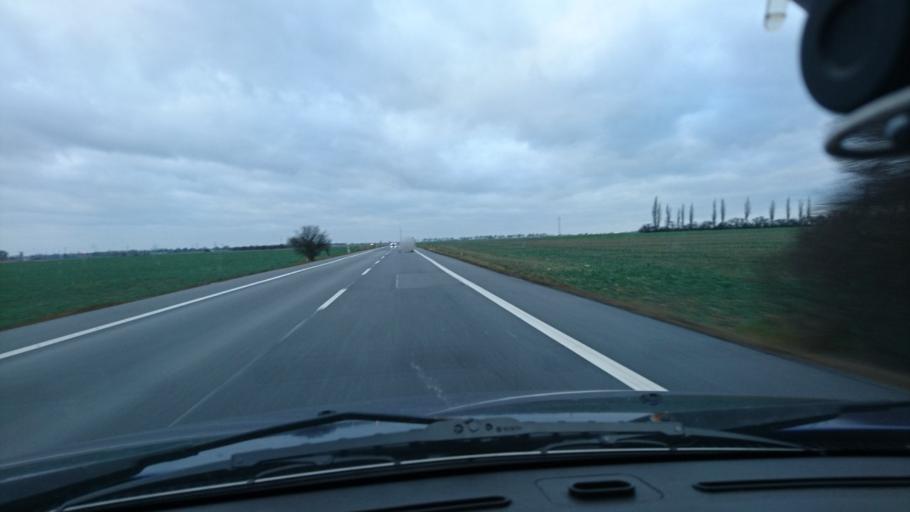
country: PL
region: Opole Voivodeship
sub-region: Powiat kluczborski
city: Kluczbork
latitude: 50.9853
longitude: 18.2402
